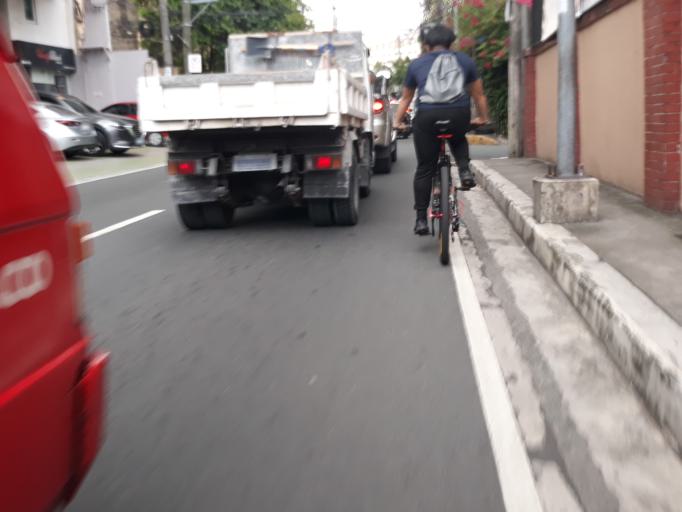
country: PH
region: Metro Manila
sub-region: San Juan
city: San Juan
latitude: 14.6007
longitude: 121.0361
